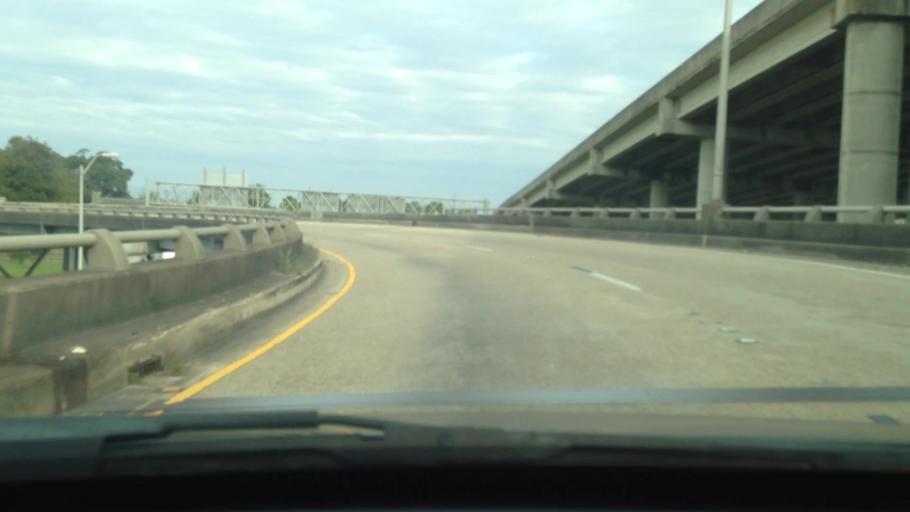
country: US
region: Louisiana
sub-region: Orleans Parish
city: New Orleans
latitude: 29.9709
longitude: -90.1100
